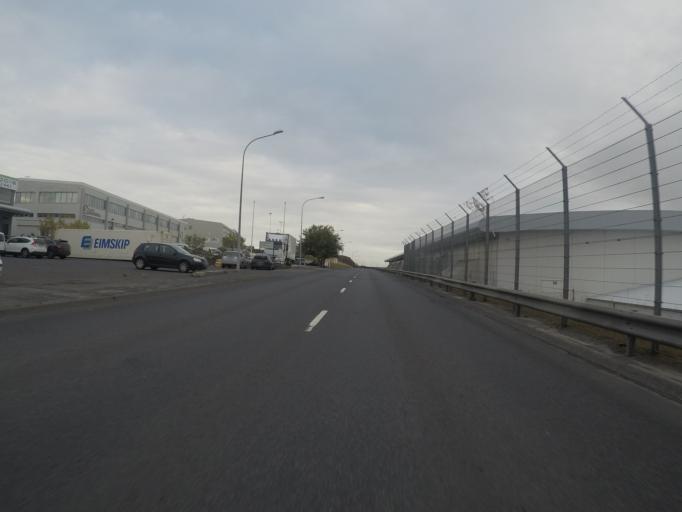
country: IS
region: Capital Region
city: Reykjavik
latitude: 64.1483
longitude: -21.8607
